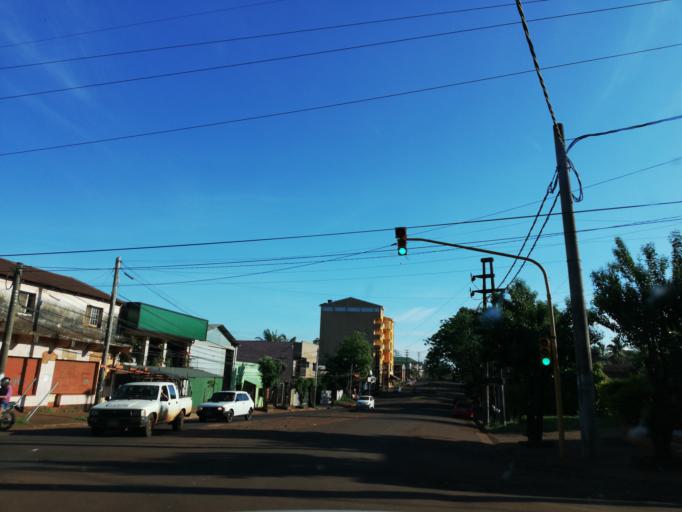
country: AR
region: Misiones
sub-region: Departamento de Obera
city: Obera
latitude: -27.5022
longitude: -55.1194
